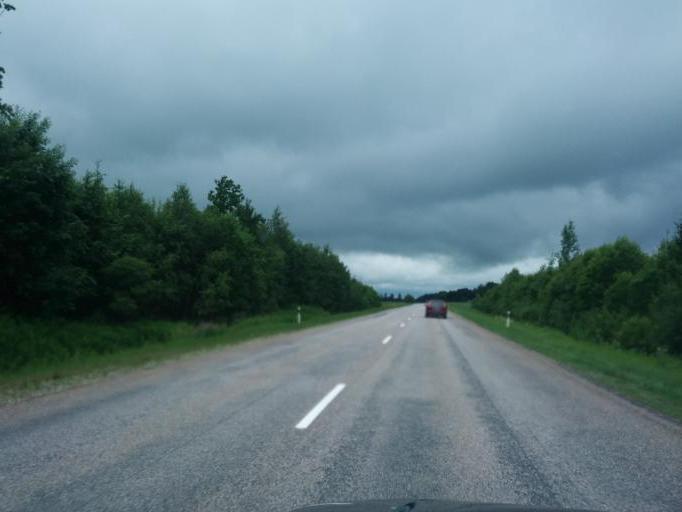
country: LV
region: Beverina
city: Murmuiza
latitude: 57.4826
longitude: 25.6089
